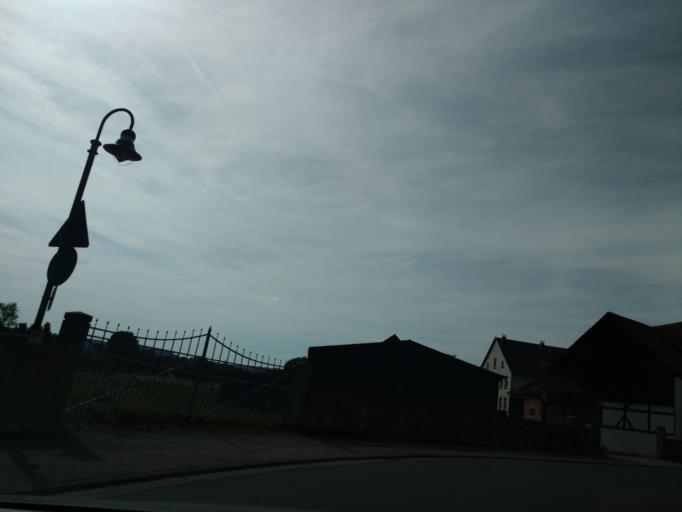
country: DE
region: Lower Saxony
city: Bad Pyrmont
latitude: 51.9827
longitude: 9.2888
